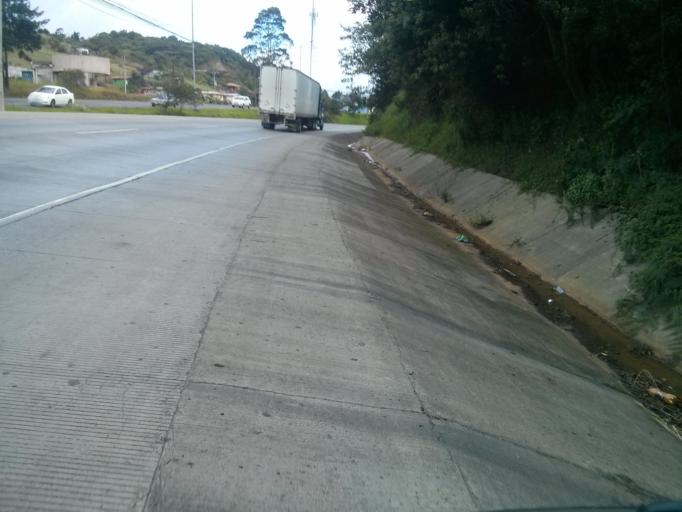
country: CR
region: Cartago
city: Tres Rios
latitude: 9.9008
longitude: -83.9472
